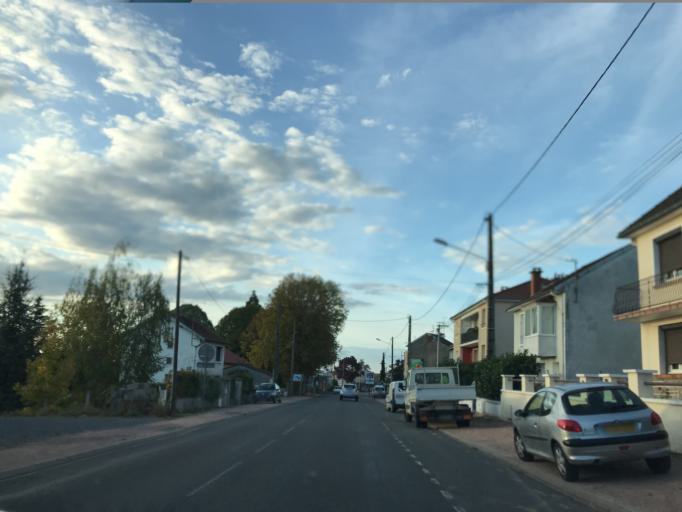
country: FR
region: Auvergne
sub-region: Departement de l'Allier
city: Abrest
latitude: 46.1114
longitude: 3.4419
